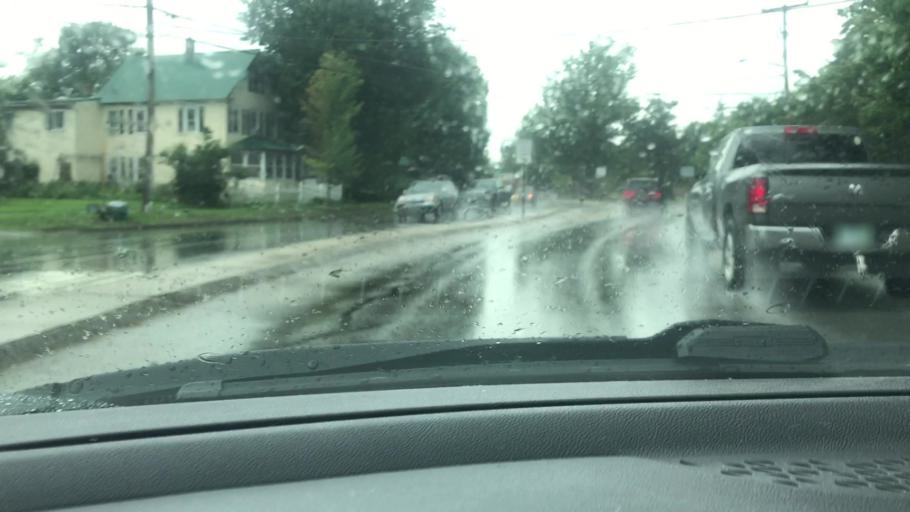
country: US
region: New Hampshire
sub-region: Merrimack County
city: Concord
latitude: 43.2158
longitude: -71.5438
